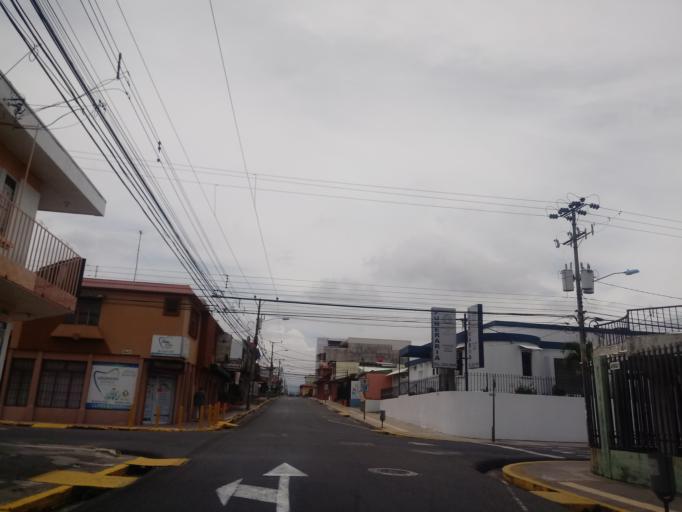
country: CR
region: Heredia
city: Heredia
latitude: 9.9999
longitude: -84.1194
